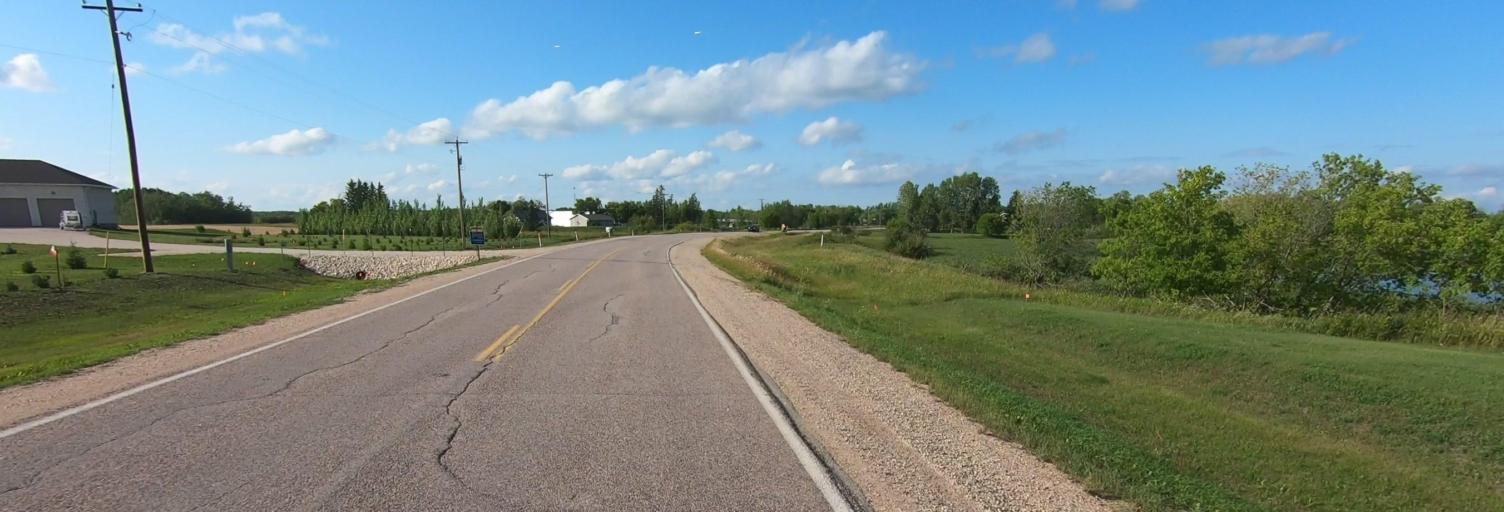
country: CA
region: Manitoba
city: Selkirk
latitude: 50.2108
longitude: -96.8413
